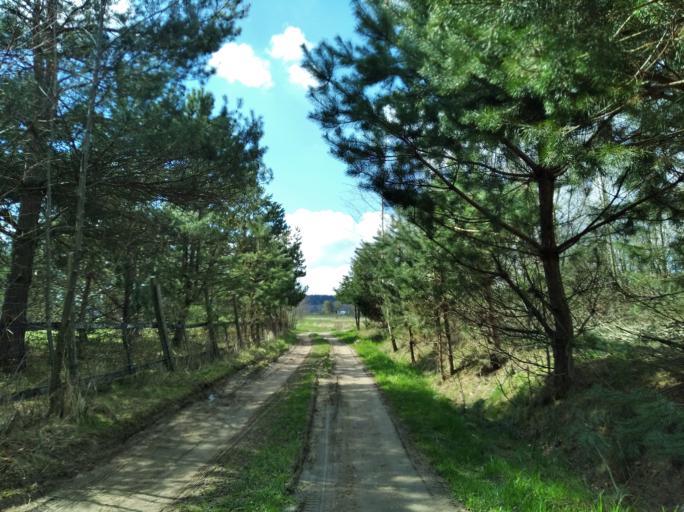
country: PL
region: Subcarpathian Voivodeship
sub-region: Powiat strzyzowski
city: Strzyzow
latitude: 49.8461
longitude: 21.7815
